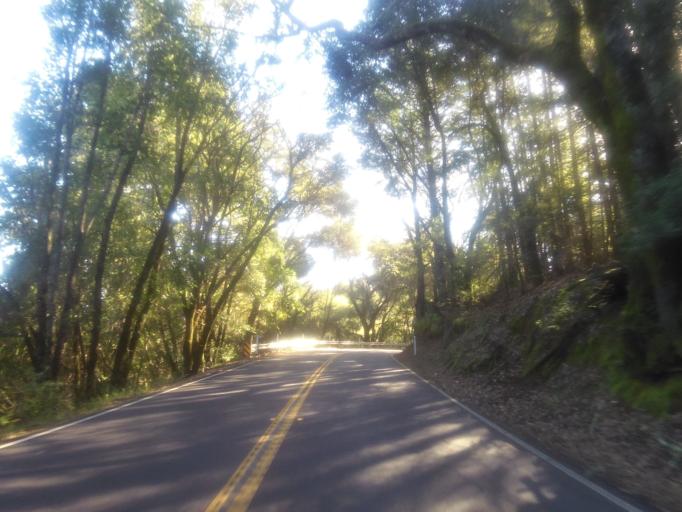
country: US
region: California
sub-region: Sonoma County
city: Cloverdale
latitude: 38.8612
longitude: -123.0827
